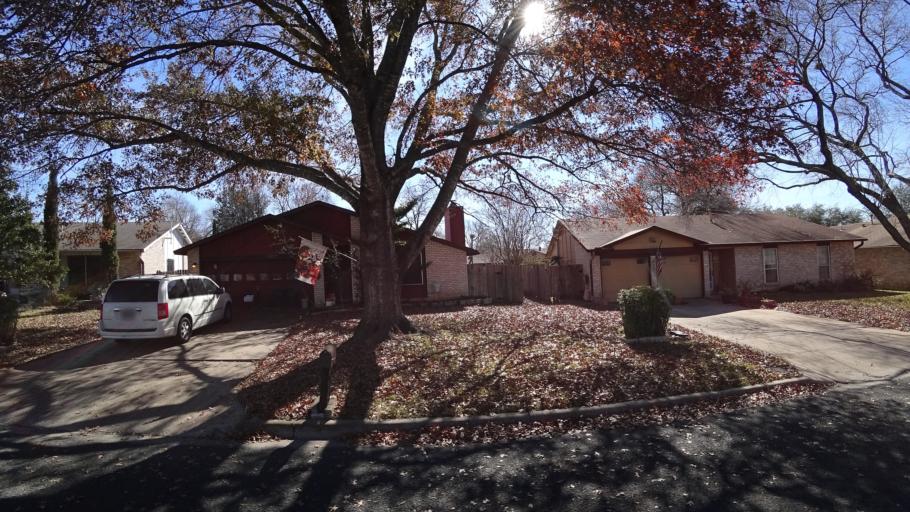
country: US
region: Texas
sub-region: Travis County
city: Wells Branch
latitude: 30.3848
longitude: -97.6989
